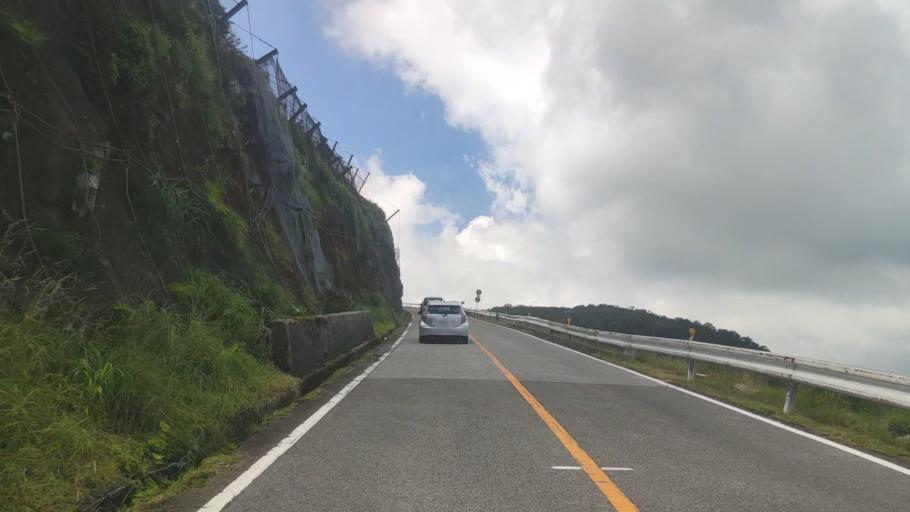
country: JP
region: Gifu
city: Tarui
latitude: 35.4289
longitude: 136.4195
